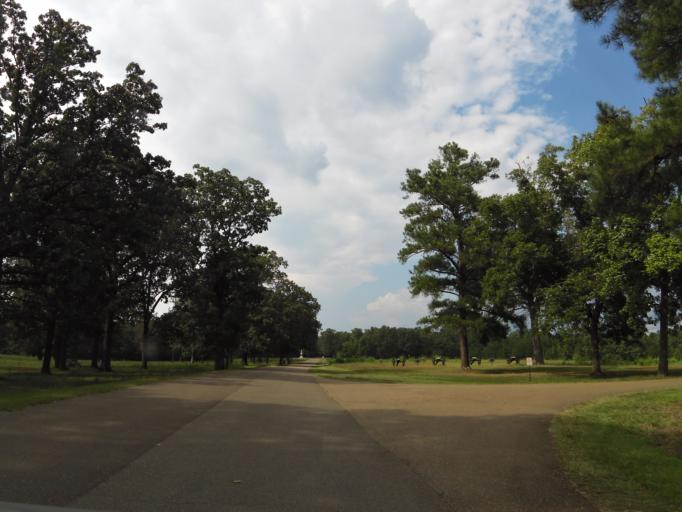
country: US
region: Tennessee
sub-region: Hardin County
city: Crump
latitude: 35.1402
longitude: -88.3321
